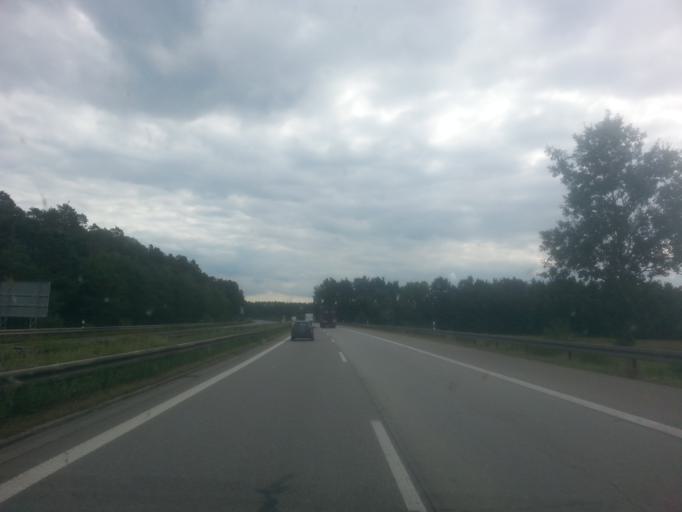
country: DE
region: Bavaria
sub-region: Upper Palatinate
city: Teublitz
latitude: 49.2626
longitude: 12.1224
